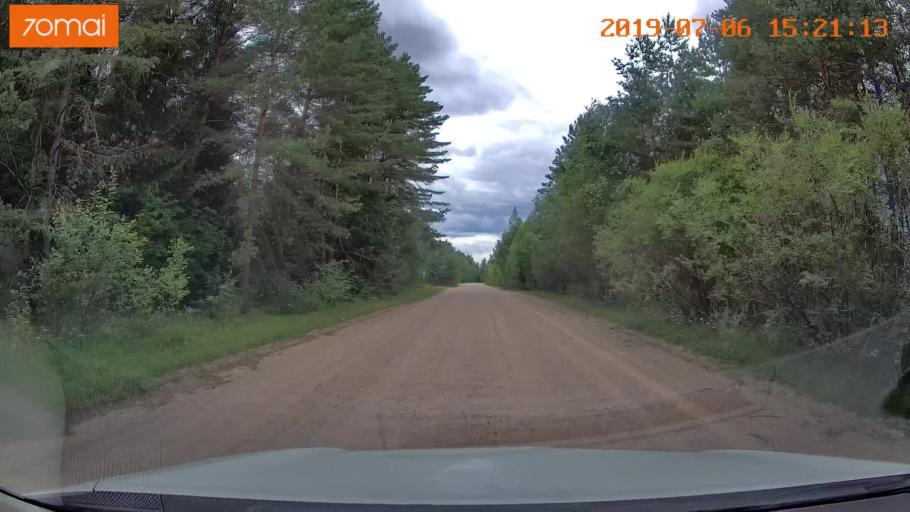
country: BY
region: Minsk
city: Valozhyn
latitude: 54.0098
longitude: 26.6190
